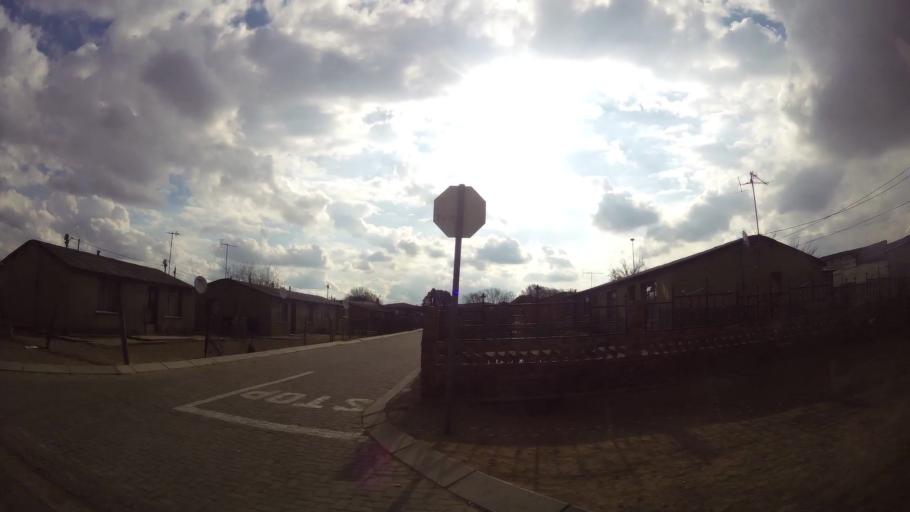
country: ZA
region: Orange Free State
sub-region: Fezile Dabi District Municipality
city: Sasolburg
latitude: -26.8397
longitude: 27.8428
